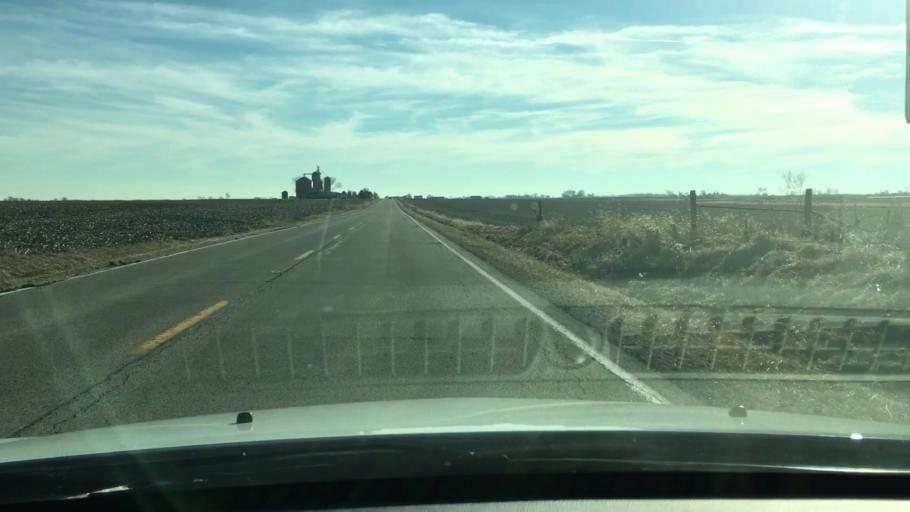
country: US
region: Illinois
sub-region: LaSalle County
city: Mendota
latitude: 41.5038
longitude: -89.1273
